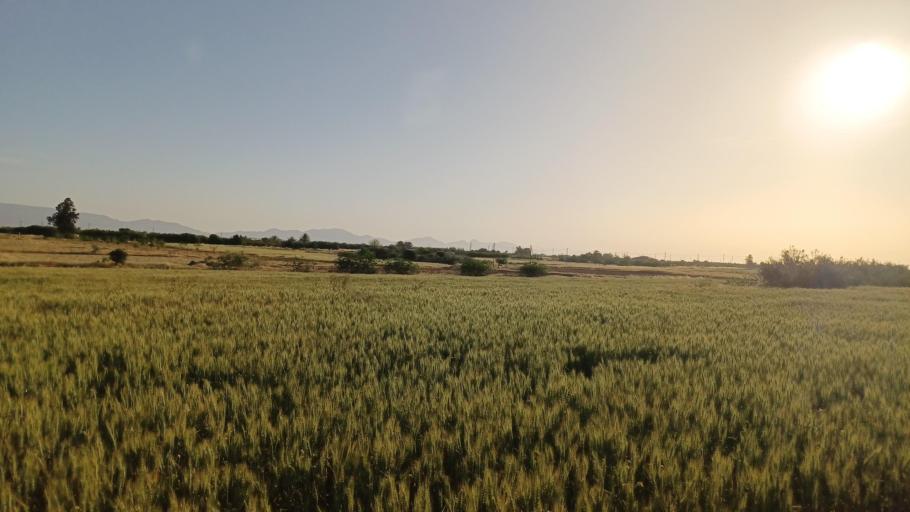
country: CY
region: Lefkosia
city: Kokkinotrimithia
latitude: 35.1486
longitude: 33.1749
